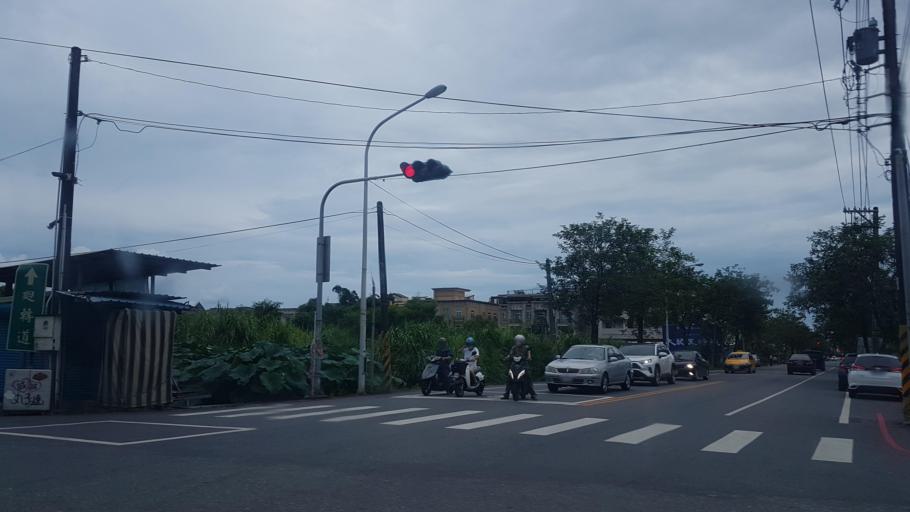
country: TW
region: Taiwan
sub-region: Hualien
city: Hualian
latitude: 23.9812
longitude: 121.5927
